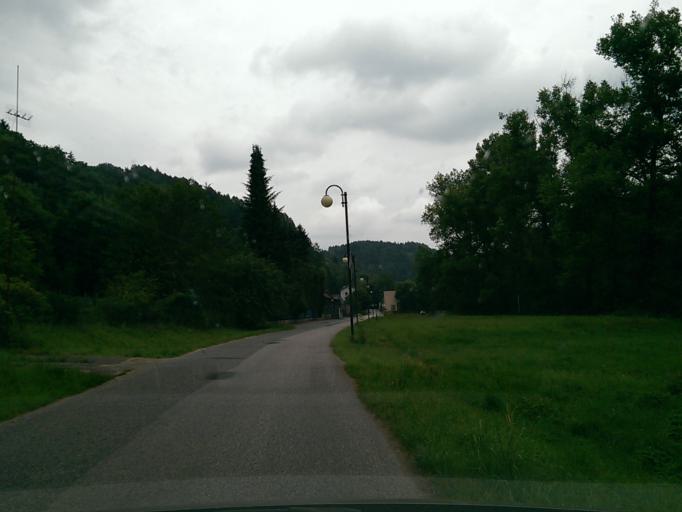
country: CZ
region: Liberecky
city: Zelezny Brod
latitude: 50.6406
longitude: 15.2697
